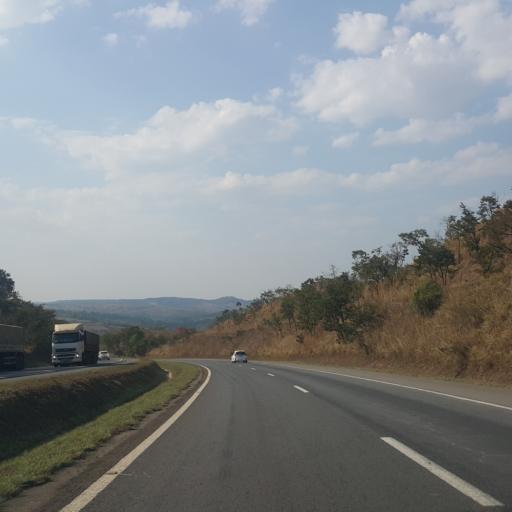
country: BR
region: Goias
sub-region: Abadiania
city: Abadiania
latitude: -16.1578
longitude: -48.6119
